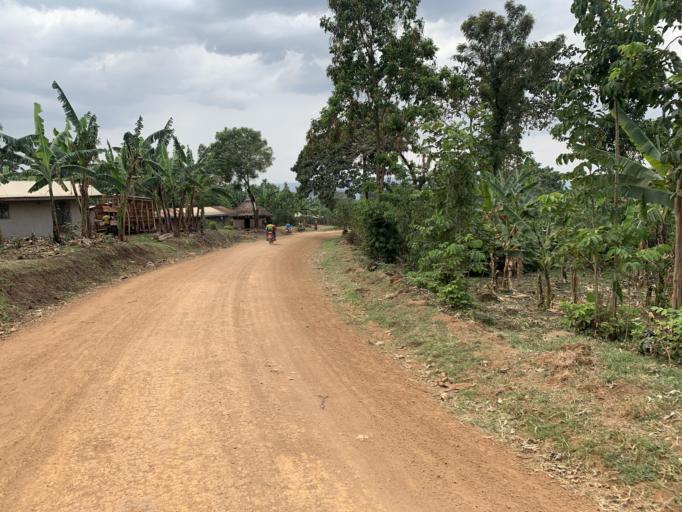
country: UG
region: Eastern Region
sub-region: Sironko District
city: Sironko
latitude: 1.2554
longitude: 34.2922
